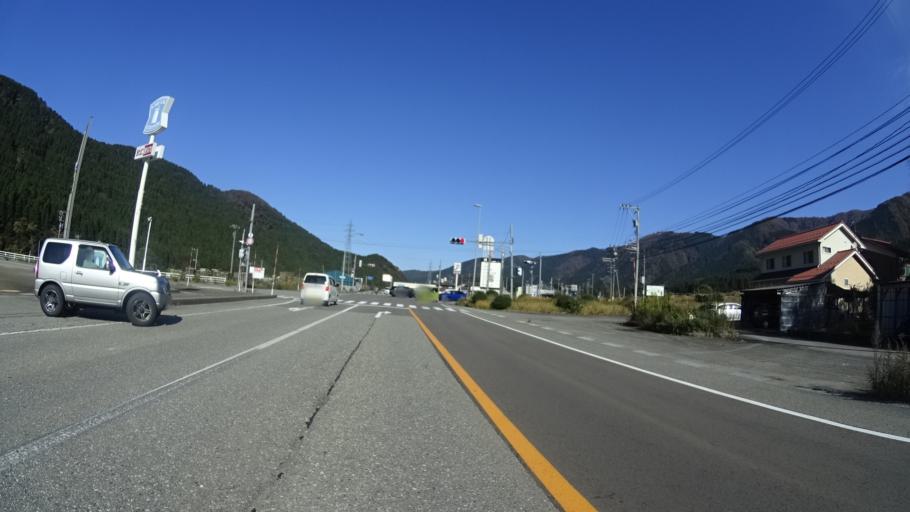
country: JP
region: Ishikawa
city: Tsurugi-asahimachi
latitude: 36.4225
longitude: 136.6312
